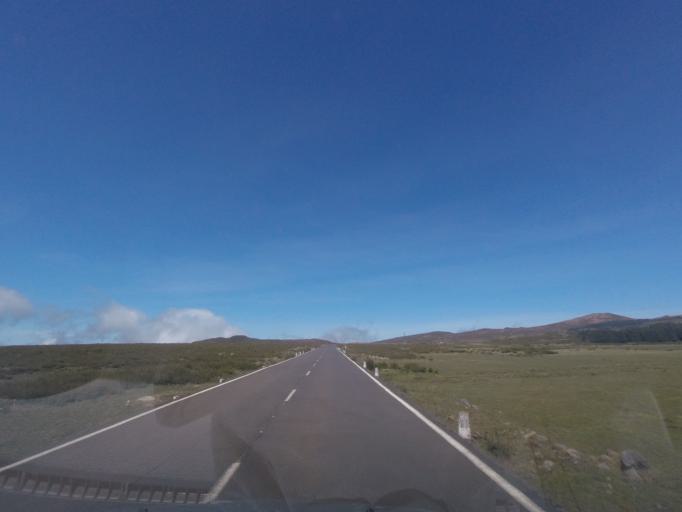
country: PT
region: Madeira
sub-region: Calheta
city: Arco da Calheta
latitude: 32.7504
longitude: -17.0985
